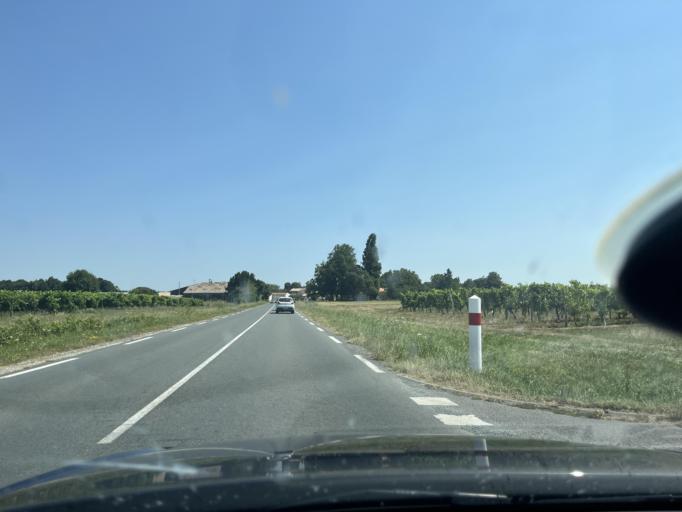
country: FR
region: Poitou-Charentes
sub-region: Departement de la Charente-Maritime
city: Cozes
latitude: 45.5477
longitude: -0.7884
